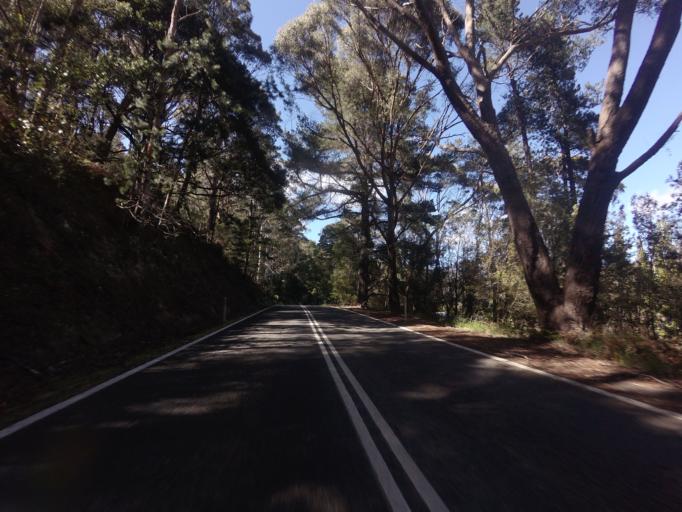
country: AU
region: Tasmania
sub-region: Derwent Valley
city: New Norfolk
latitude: -42.6993
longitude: 146.7138
